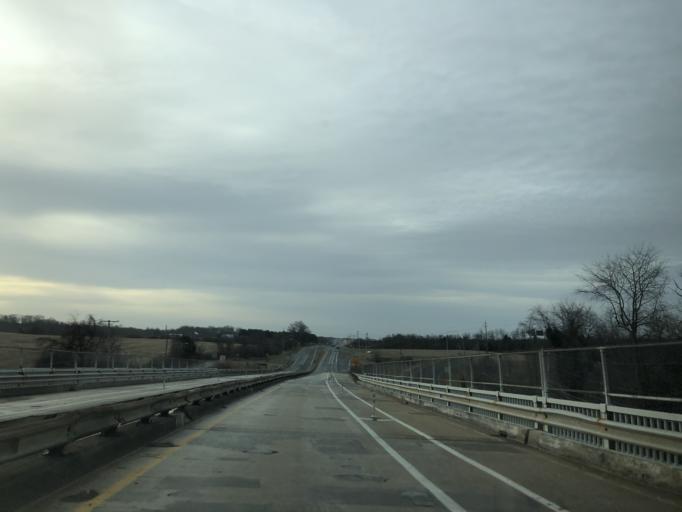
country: US
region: Delaware
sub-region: New Castle County
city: Delaware City
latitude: 39.5479
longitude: -75.6487
